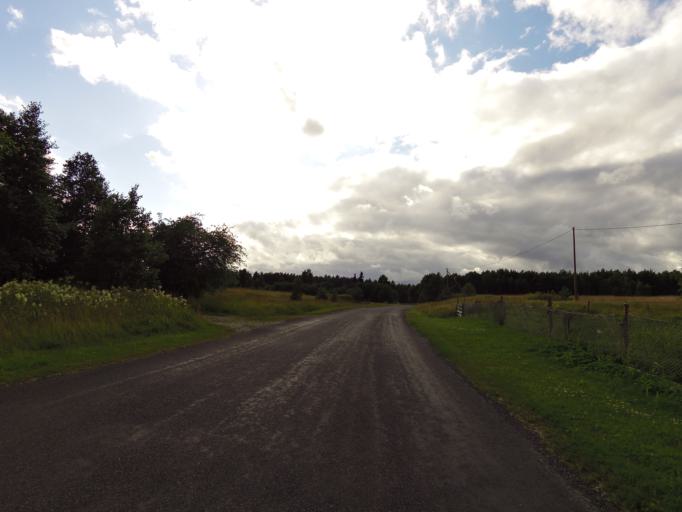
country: EE
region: Laeaene
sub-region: Vormsi vald
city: Hullo
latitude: 58.9847
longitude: 23.2966
